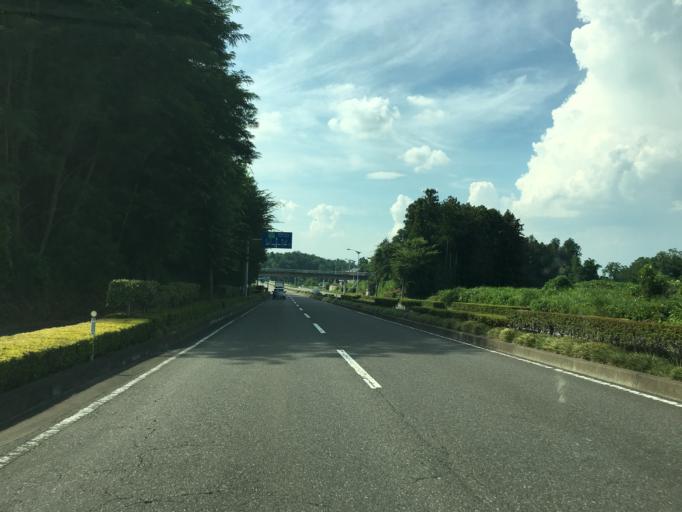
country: JP
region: Fukushima
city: Sukagawa
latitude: 37.2603
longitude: 140.4200
